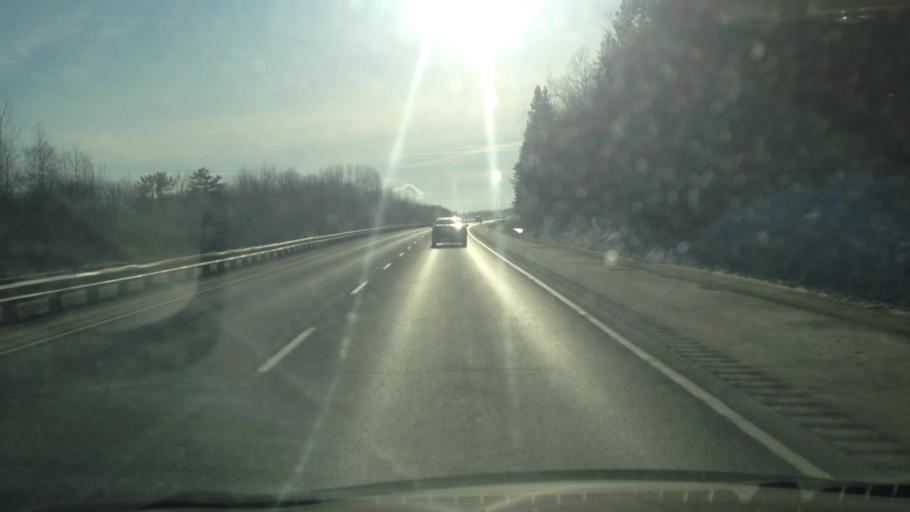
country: CA
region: Quebec
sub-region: Laurentides
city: Prevost
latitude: 45.8523
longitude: -74.0757
